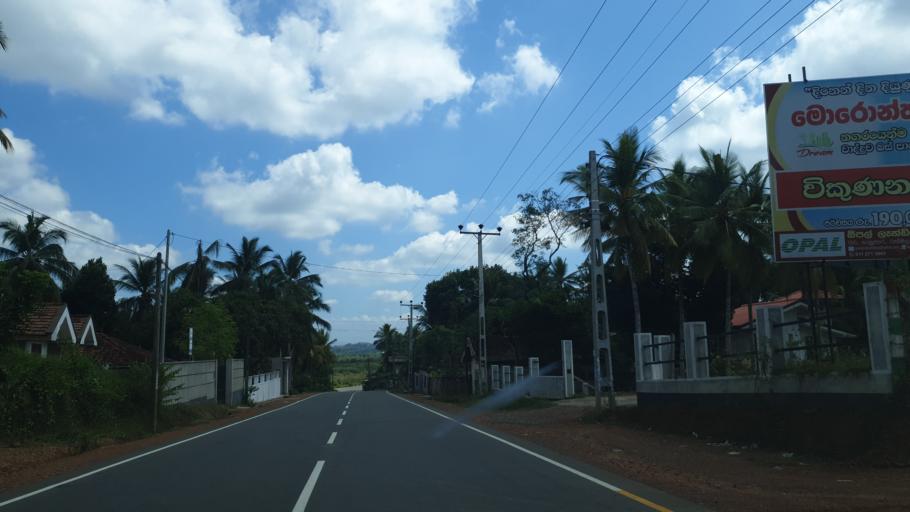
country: LK
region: Western
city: Panadura
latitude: 6.6657
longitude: 79.9652
